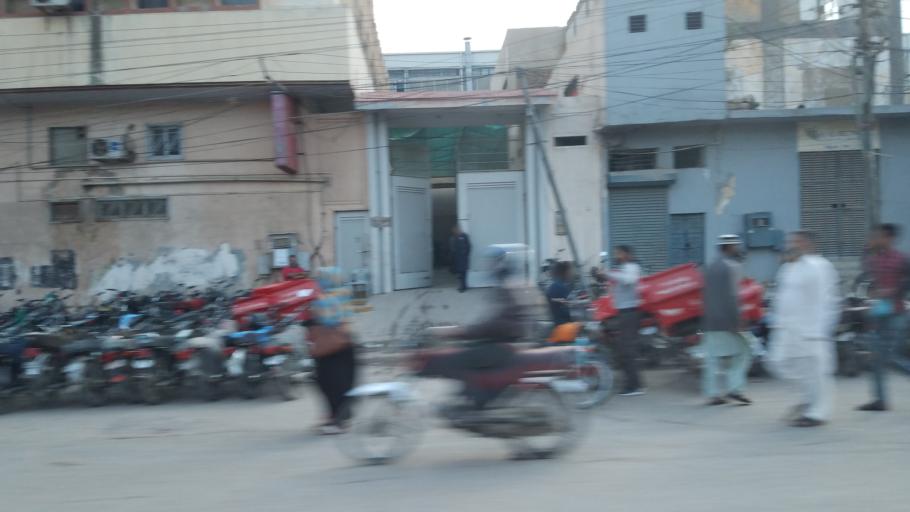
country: PK
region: Sindh
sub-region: Karachi District
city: Karachi
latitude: 24.9374
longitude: 67.0854
